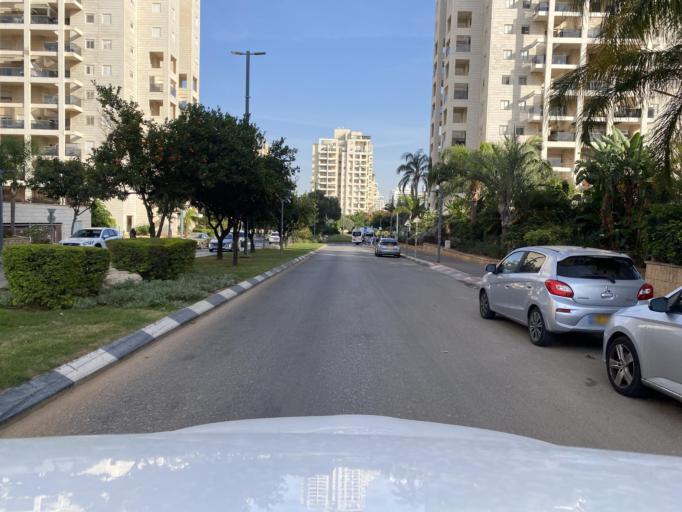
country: IL
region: Tel Aviv
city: Giv`at Shemu'el
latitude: 32.0730
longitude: 34.8523
